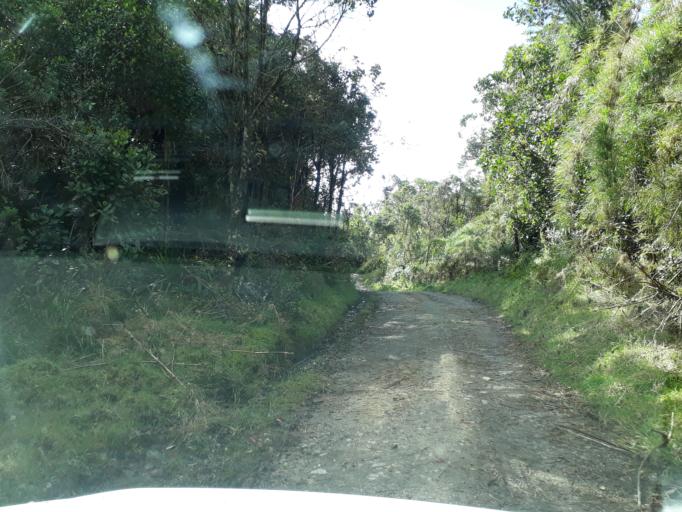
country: CO
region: Cundinamarca
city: Guasca
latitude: 4.8009
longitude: -73.7829
